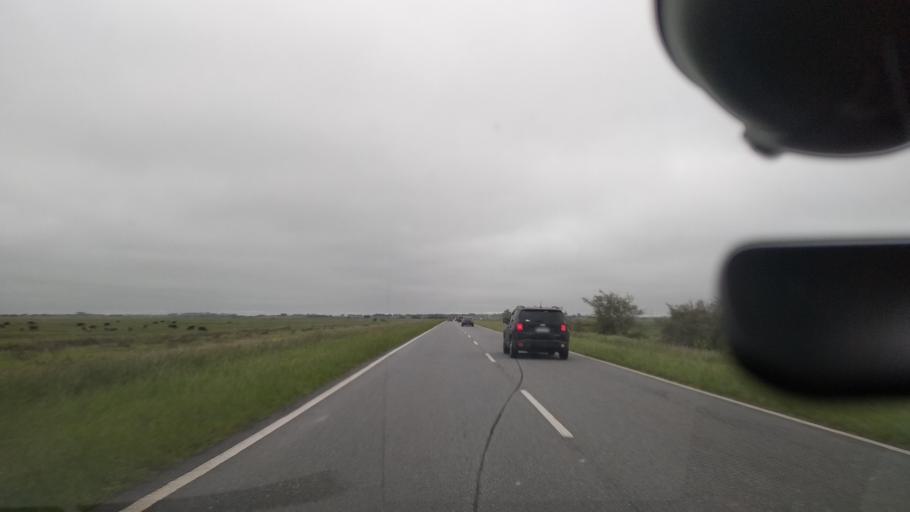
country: AR
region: Buenos Aires
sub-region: Partido de Magdalena
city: Magdalena
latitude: -35.2574
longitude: -57.6555
